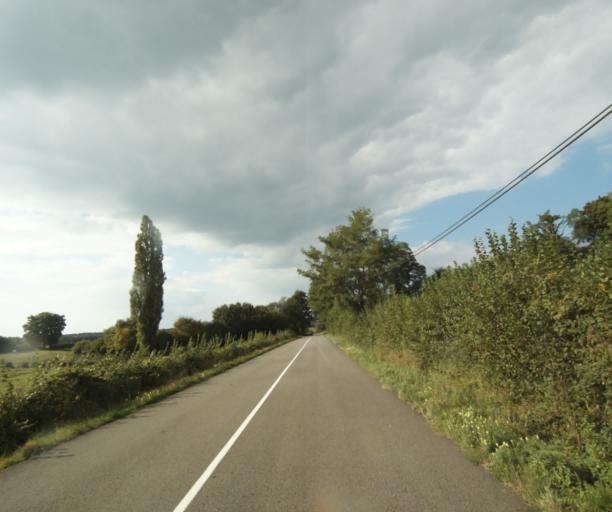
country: FR
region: Bourgogne
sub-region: Departement de Saone-et-Loire
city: Palinges
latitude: 46.5129
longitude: 4.2578
